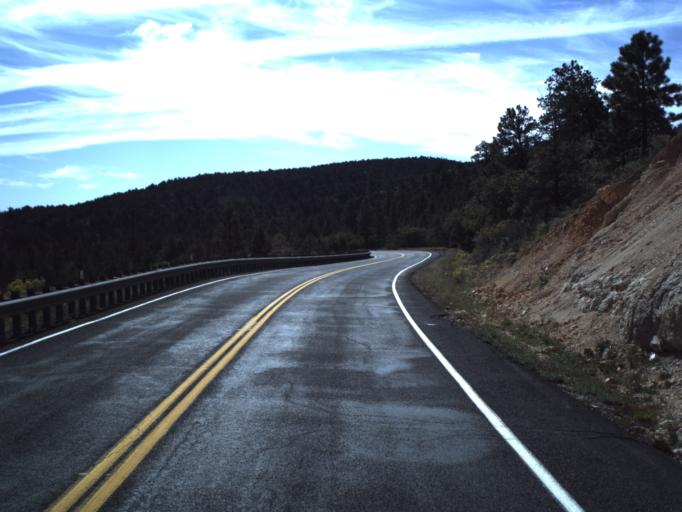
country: US
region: Utah
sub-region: Garfield County
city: Panguitch
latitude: 37.6650
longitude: -112.1096
